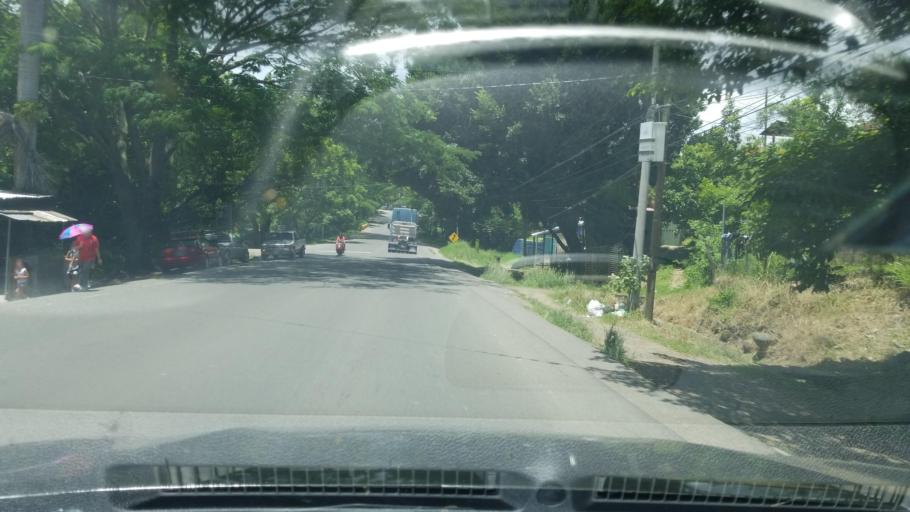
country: HN
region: Francisco Morazan
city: Rio Abajo
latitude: 14.1709
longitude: -87.2072
